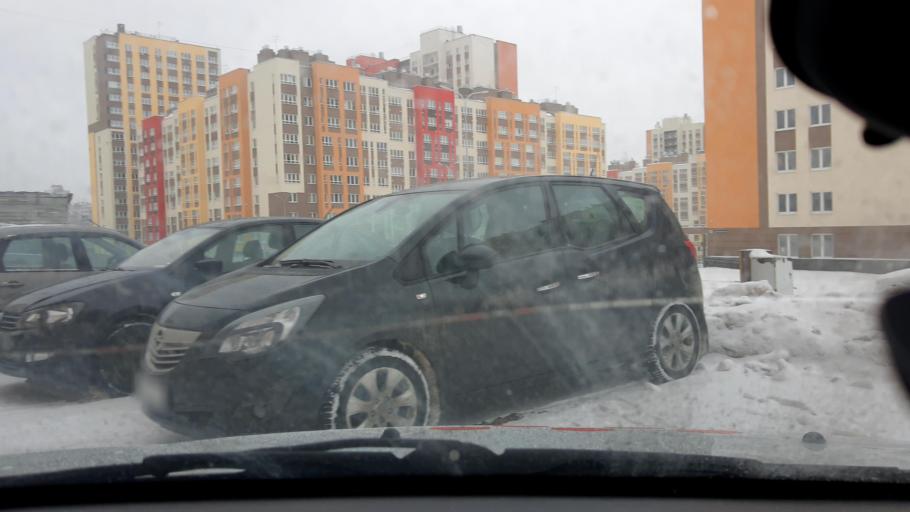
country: RU
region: Nizjnij Novgorod
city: Afonino
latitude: 56.2742
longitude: 44.0484
